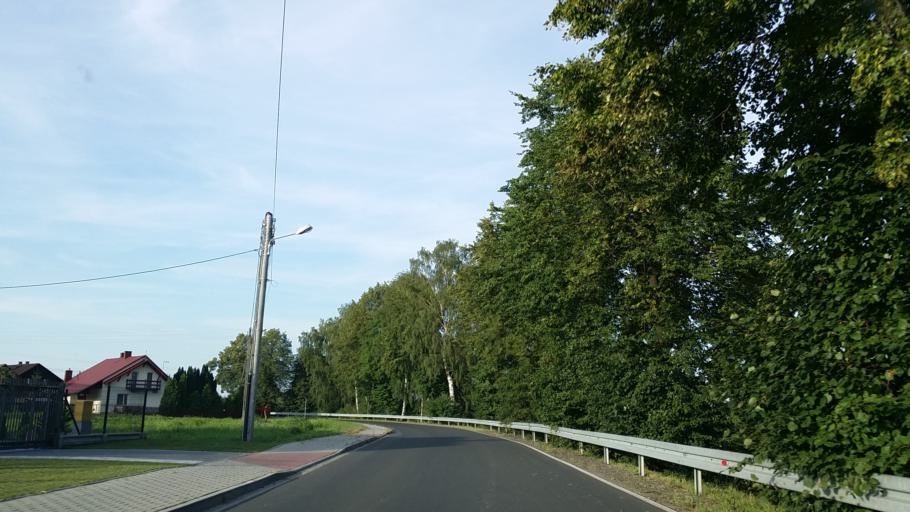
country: PL
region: Lesser Poland Voivodeship
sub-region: Powiat oswiecimski
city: Zator
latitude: 49.9895
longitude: 19.4203
